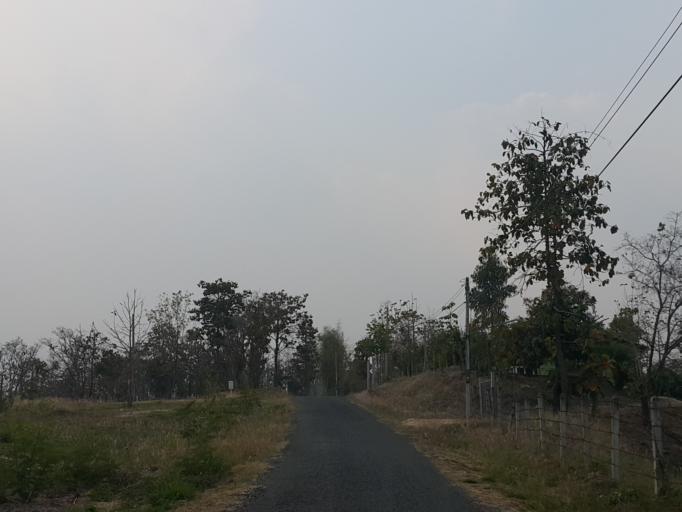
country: TH
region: Chiang Mai
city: Mae Taeng
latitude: 18.9691
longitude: 98.9322
